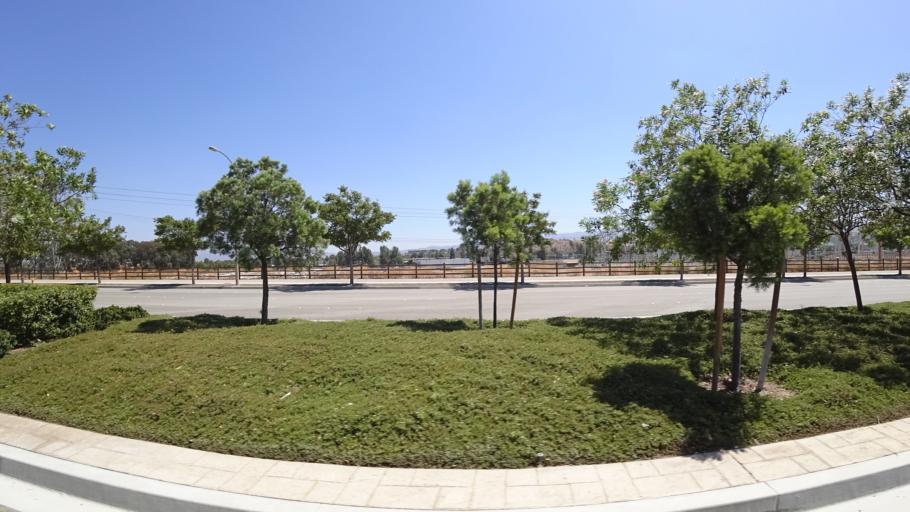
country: US
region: California
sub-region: Los Angeles County
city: Valencia
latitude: 34.4425
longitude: -118.5817
